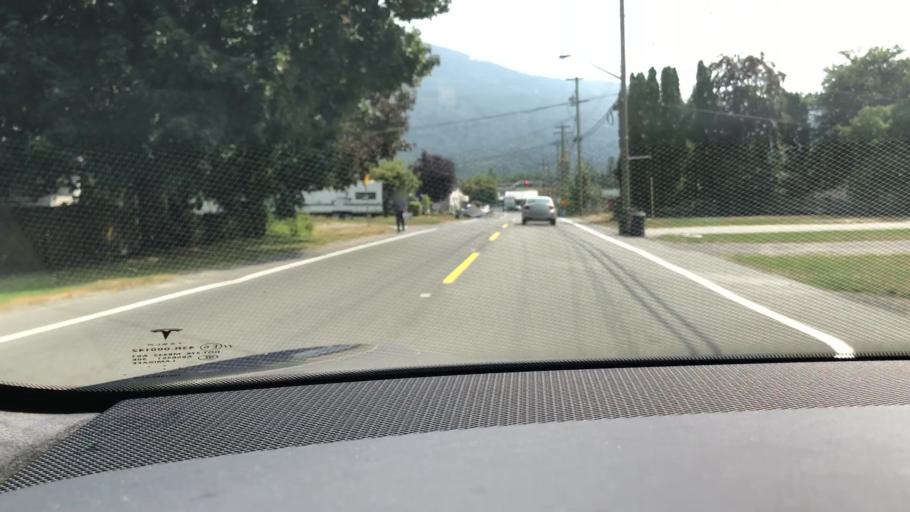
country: CA
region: British Columbia
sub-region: Fraser Valley Regional District
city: Chilliwack
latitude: 49.0837
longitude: -122.0649
